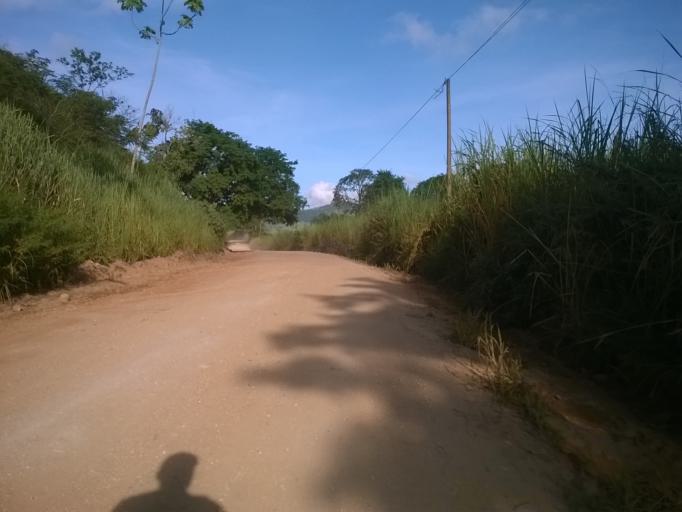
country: BR
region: Minas Gerais
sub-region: Uba
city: Uba
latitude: -21.0800
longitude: -42.9841
